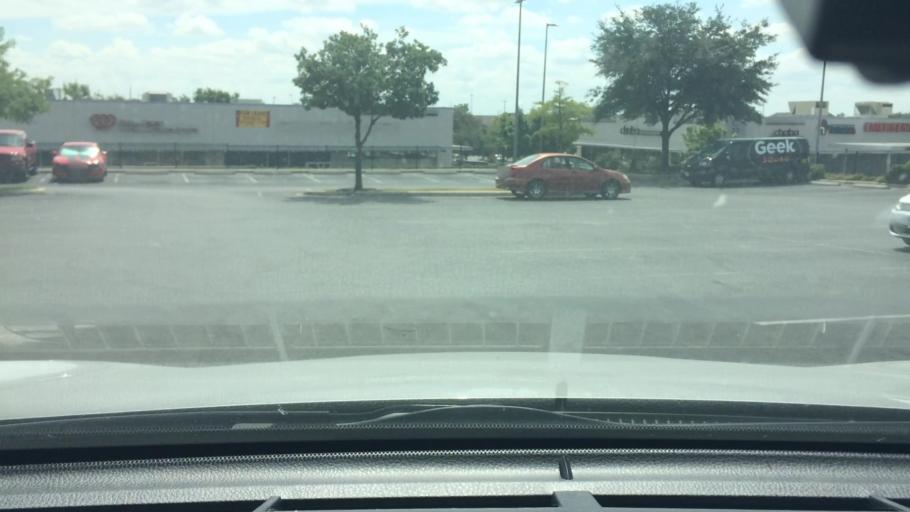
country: US
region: Texas
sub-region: Bexar County
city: San Antonio
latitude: 29.3501
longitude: -98.4363
